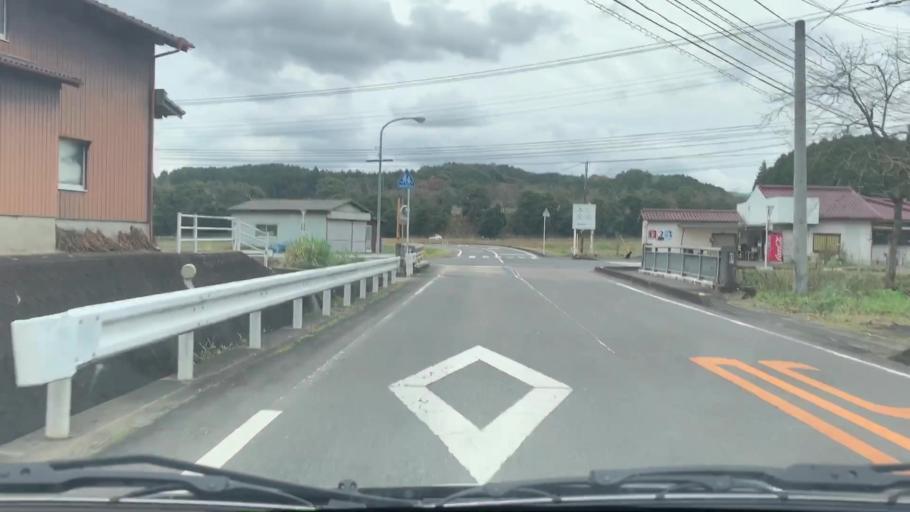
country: JP
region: Saga Prefecture
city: Ureshinomachi-shimojuku
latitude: 33.1277
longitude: 129.9800
